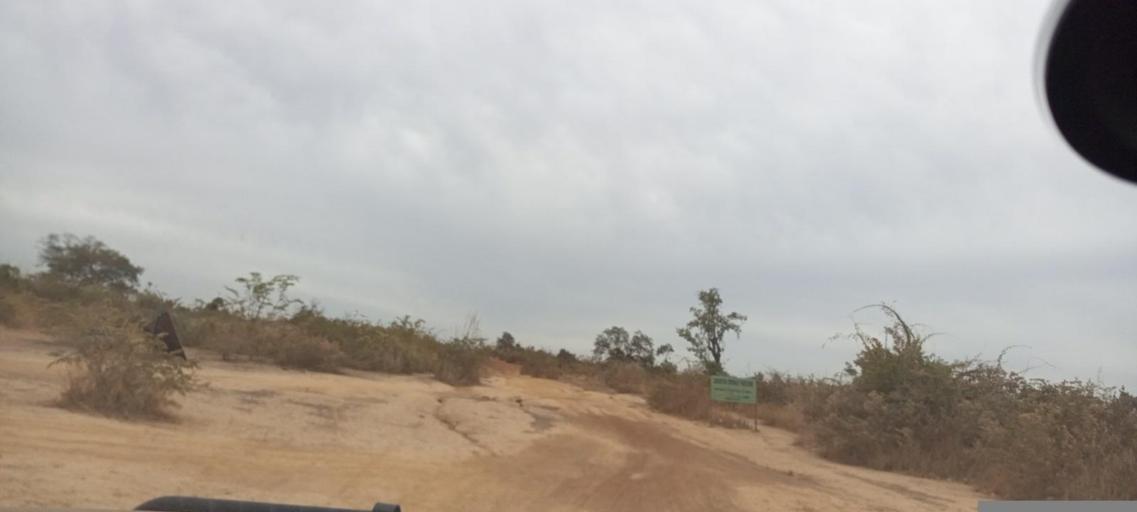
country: ML
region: Koulikoro
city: Kati
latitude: 12.7889
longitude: -8.2564
